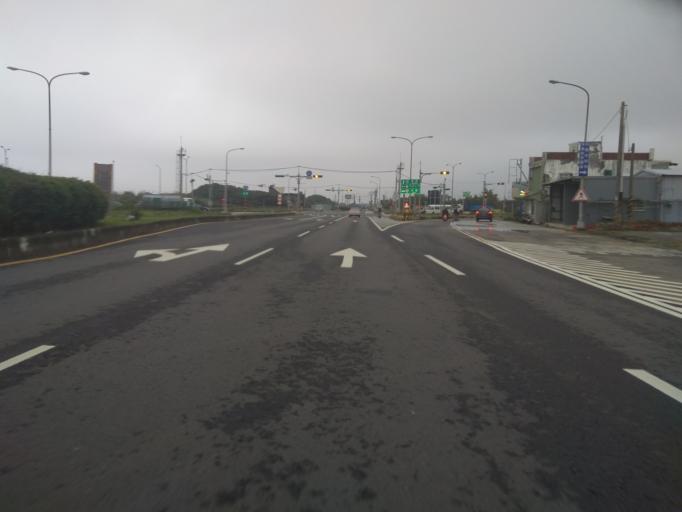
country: TW
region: Taiwan
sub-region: Hsinchu
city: Zhubei
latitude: 25.0259
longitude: 121.0631
